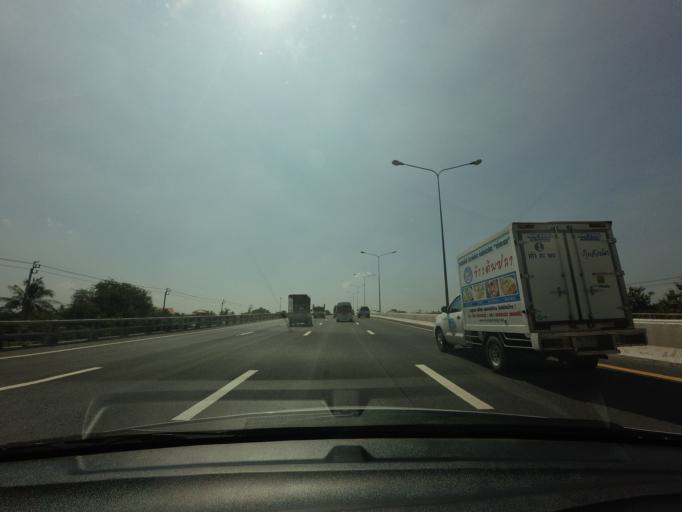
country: TH
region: Bangkok
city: Lat Krabang
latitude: 13.7159
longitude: 100.8174
